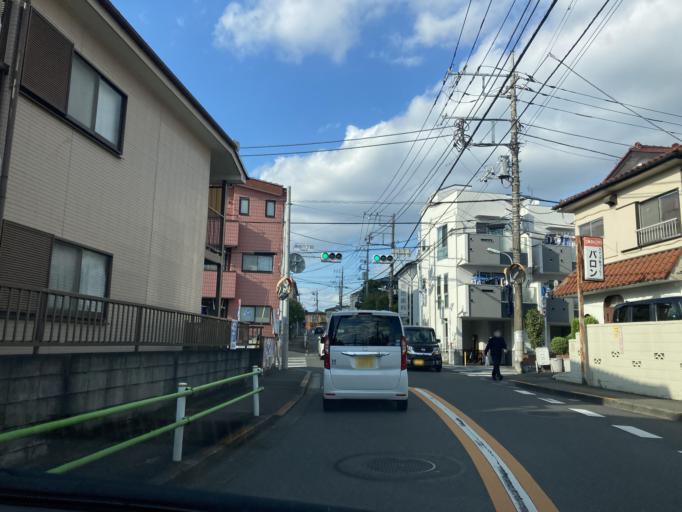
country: JP
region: Tokyo
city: Chofugaoka
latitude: 35.6436
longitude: 139.5512
